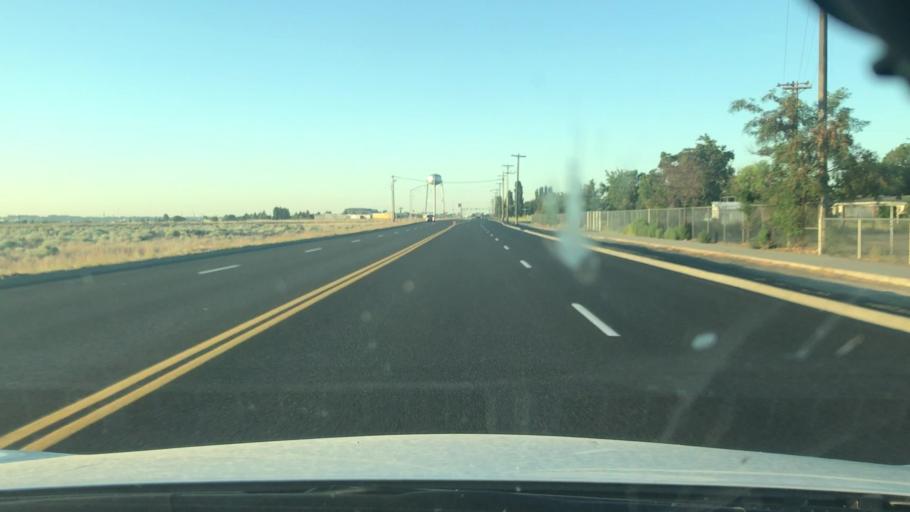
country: US
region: Washington
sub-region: Grant County
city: Moses Lake North
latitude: 47.1691
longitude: -119.3161
